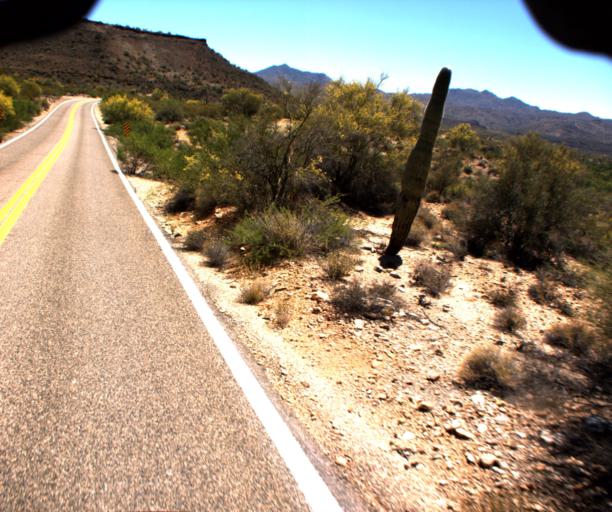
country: US
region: Arizona
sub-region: Yavapai County
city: Bagdad
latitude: 34.4961
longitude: -113.0664
